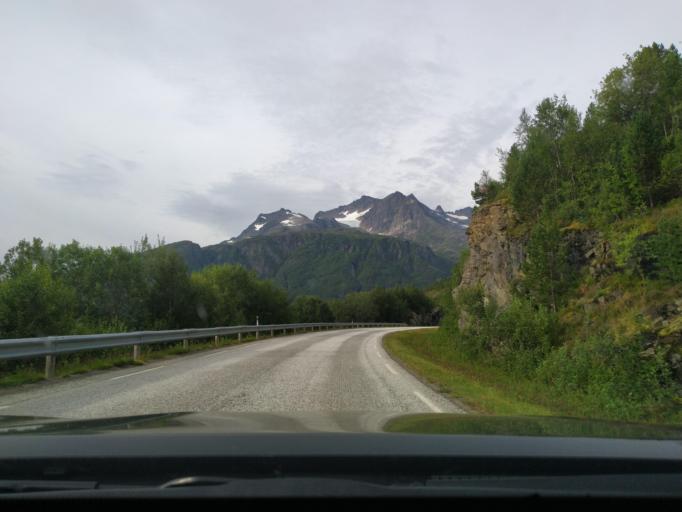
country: NO
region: Troms
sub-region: Dyroy
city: Brostadbotn
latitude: 68.9001
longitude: 17.4777
